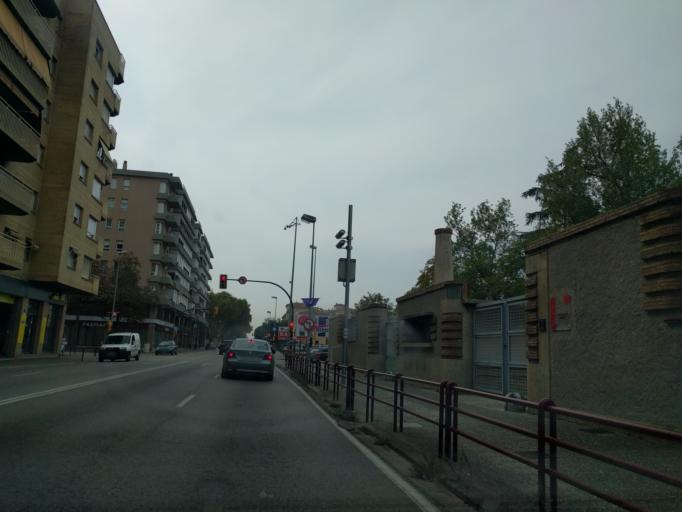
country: ES
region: Catalonia
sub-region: Provincia de Girona
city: Girona
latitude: 41.9761
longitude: 2.8168
